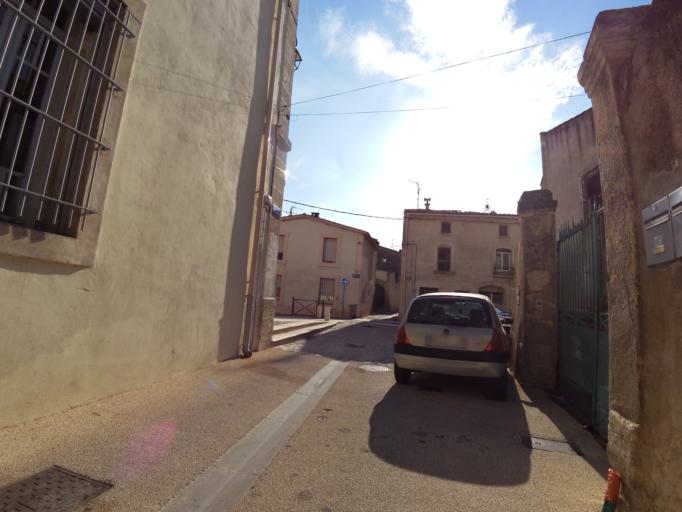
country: FR
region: Languedoc-Roussillon
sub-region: Departement de l'Herault
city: Lunel-Viel
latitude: 43.6778
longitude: 4.0929
